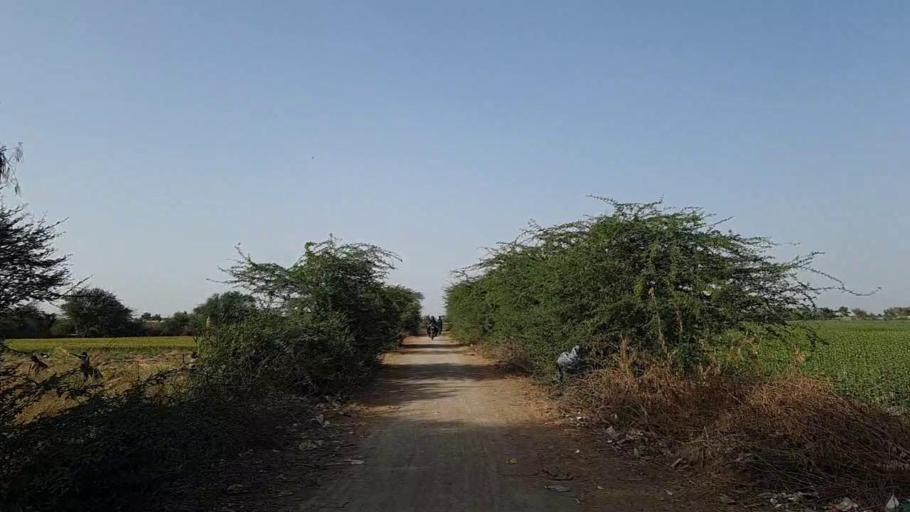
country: PK
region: Sindh
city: Jati
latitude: 24.2838
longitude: 68.1512
